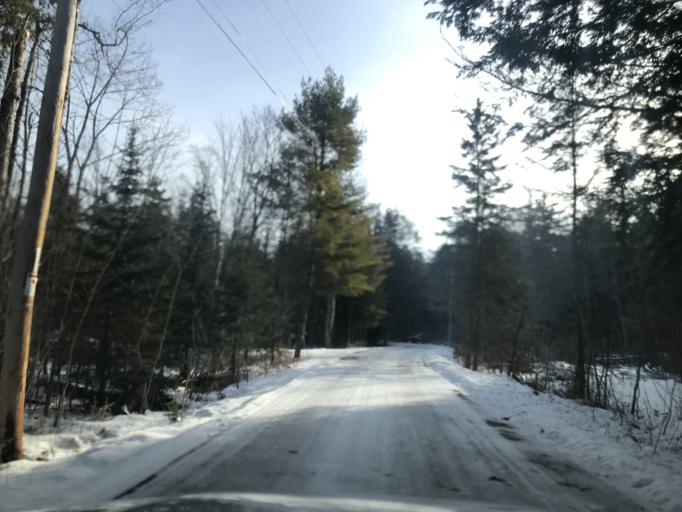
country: US
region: Wisconsin
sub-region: Door County
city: Sturgeon Bay
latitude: 45.1505
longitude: -87.0385
